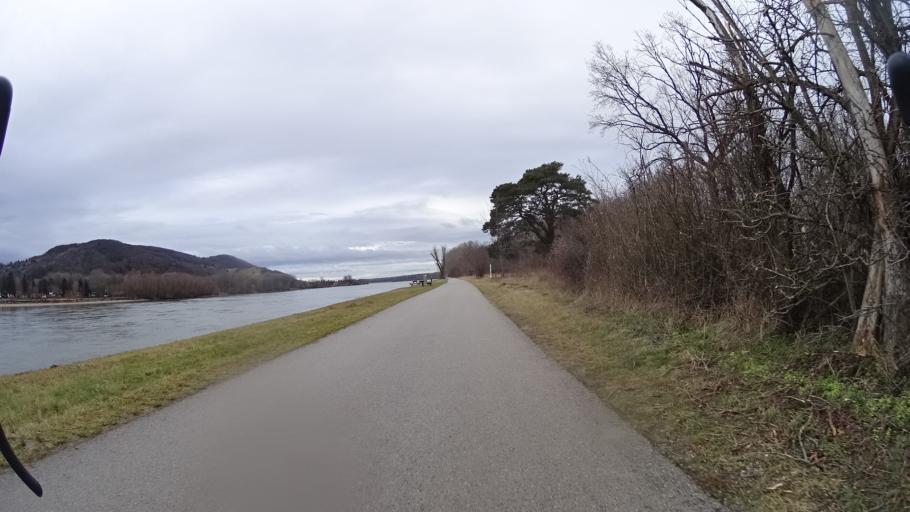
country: AT
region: Lower Austria
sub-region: Politischer Bezirk Korneuburg
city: Korneuburg
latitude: 48.3449
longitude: 16.3056
